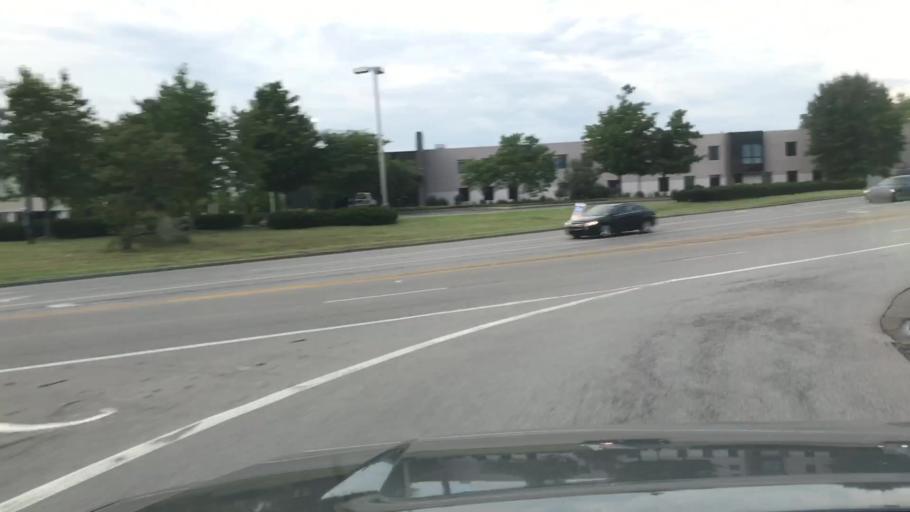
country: US
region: Tennessee
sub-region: Rutherford County
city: La Vergne
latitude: 36.0446
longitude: -86.6507
